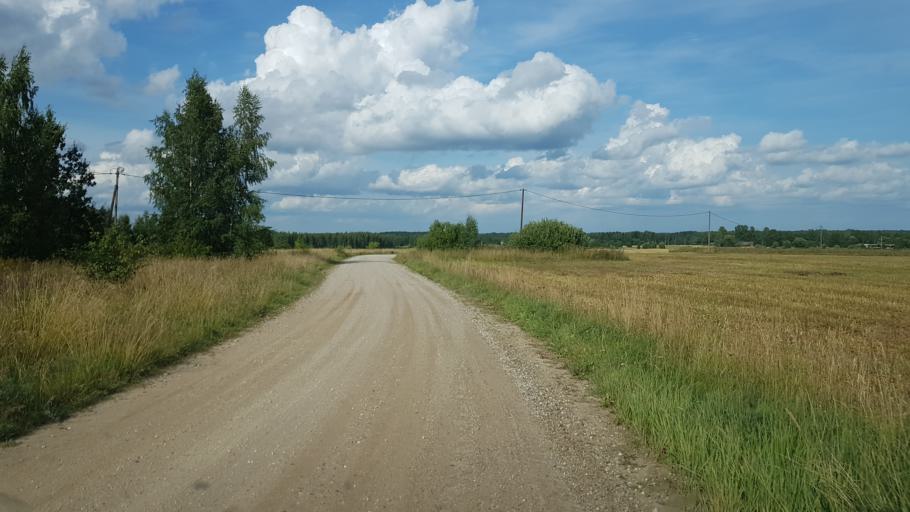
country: RU
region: Pskov
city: Pechory
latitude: 57.7979
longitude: 27.5010
